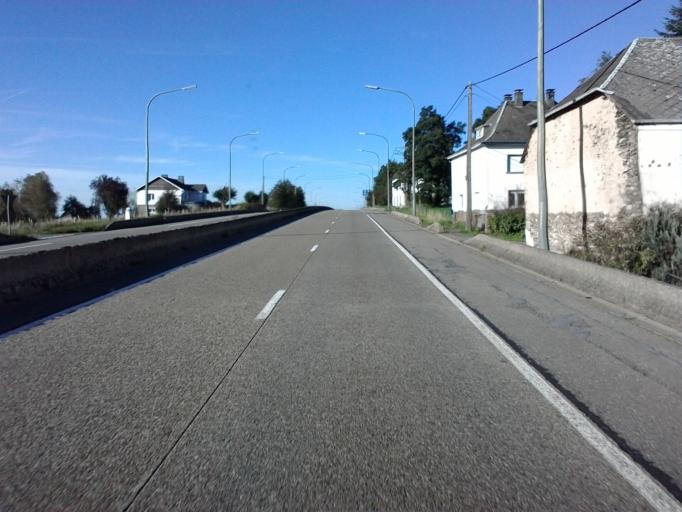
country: BE
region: Wallonia
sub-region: Province du Luxembourg
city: Fauvillers
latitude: 49.9210
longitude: 5.7039
